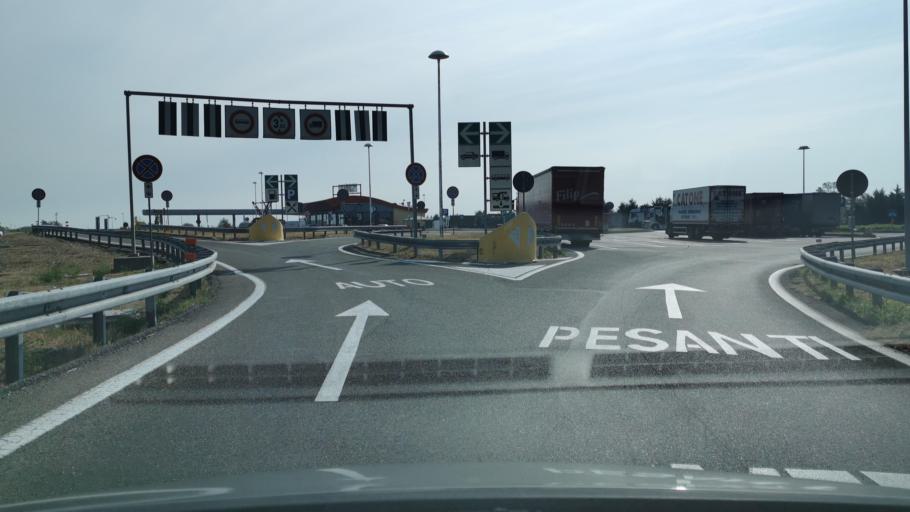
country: IT
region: Emilia-Romagna
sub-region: Provincia di Piacenza
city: San Nicolo
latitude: 45.0611
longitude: 9.6505
